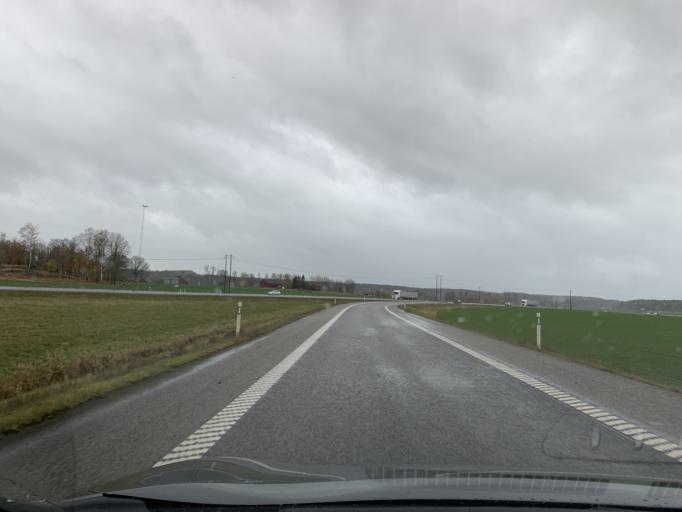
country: SE
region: Soedermanland
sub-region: Nykopings Kommun
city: Nykoping
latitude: 58.7501
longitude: 16.9689
